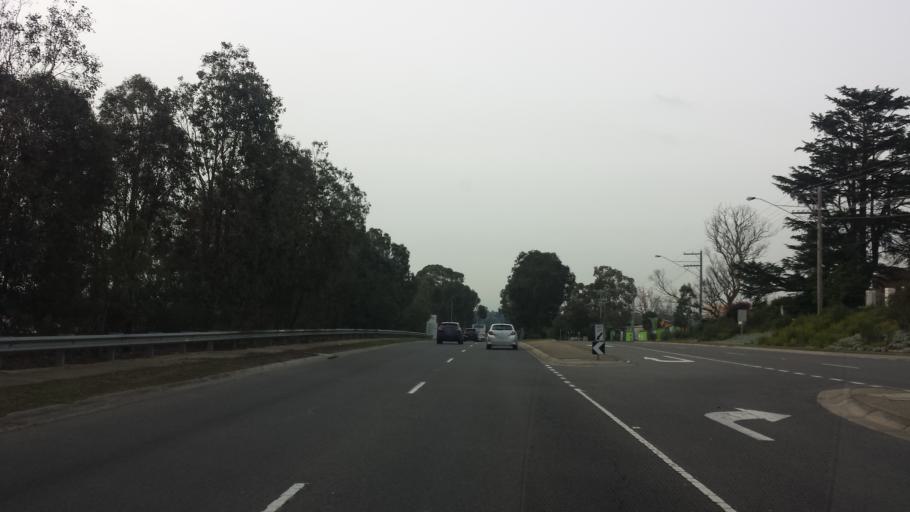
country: AU
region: Victoria
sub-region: Manningham
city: Doncaster
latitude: -37.7757
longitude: 145.1256
